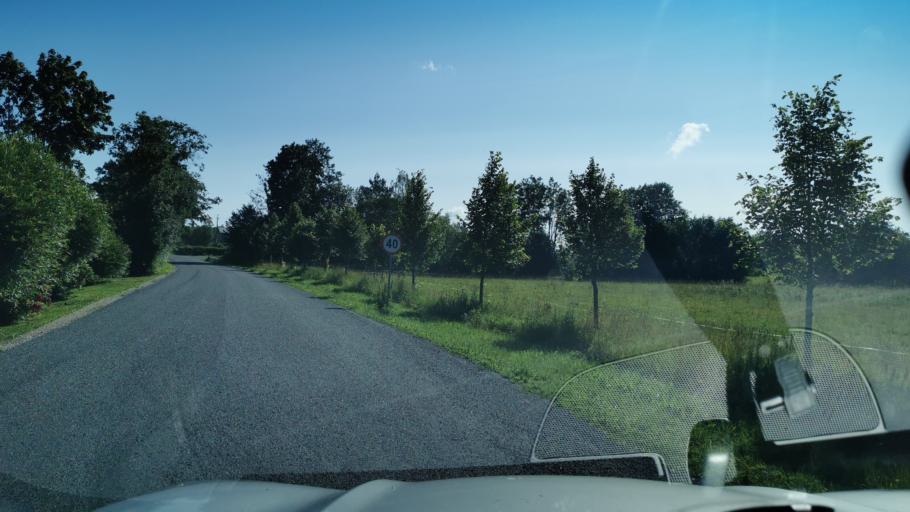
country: EE
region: Harju
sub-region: Paldiski linn
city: Paldiski
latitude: 59.2076
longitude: 24.0111
